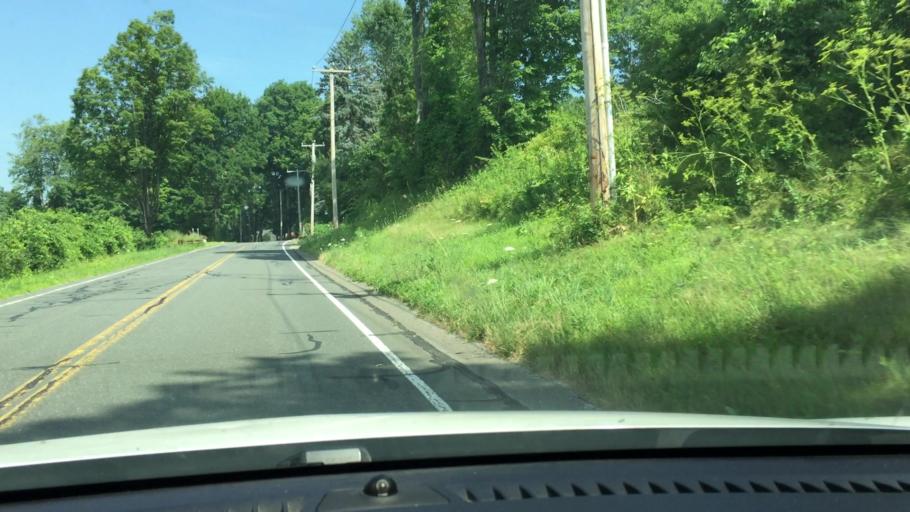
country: US
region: Massachusetts
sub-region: Berkshire County
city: Lee
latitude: 42.2266
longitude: -73.1875
